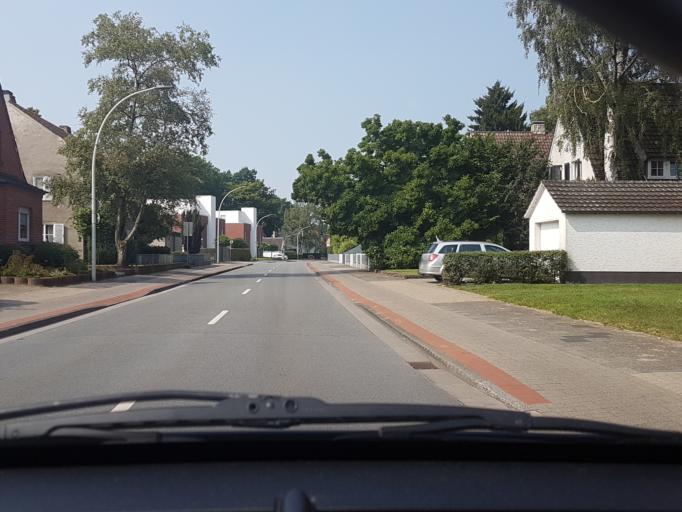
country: DE
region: North Rhine-Westphalia
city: Emsdetten
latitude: 52.1673
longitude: 7.5362
